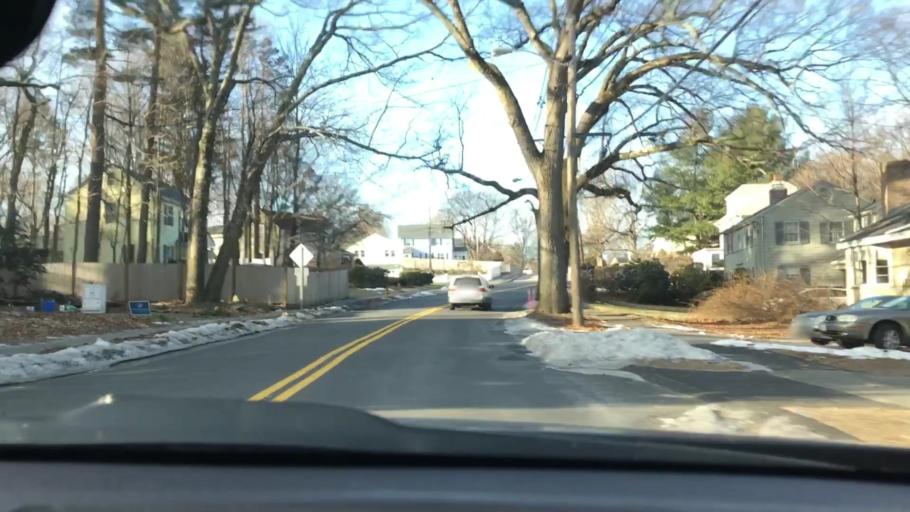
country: US
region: Massachusetts
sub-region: Norfolk County
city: Needham
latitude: 42.2962
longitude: -71.2258
